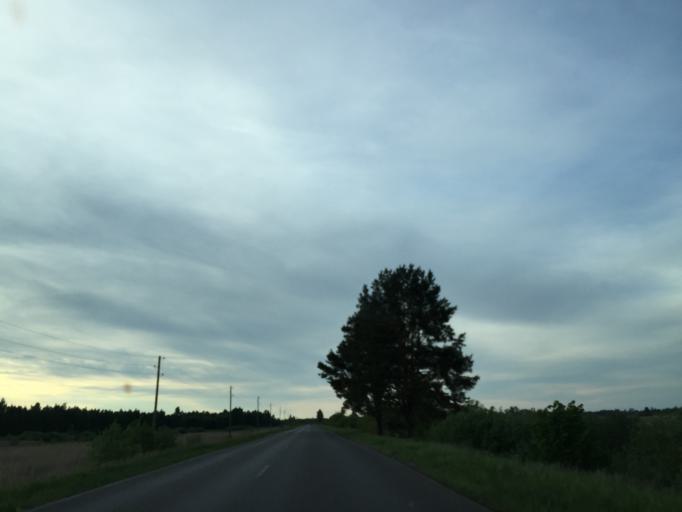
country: LV
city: Tireli
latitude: 56.8195
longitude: 23.5702
